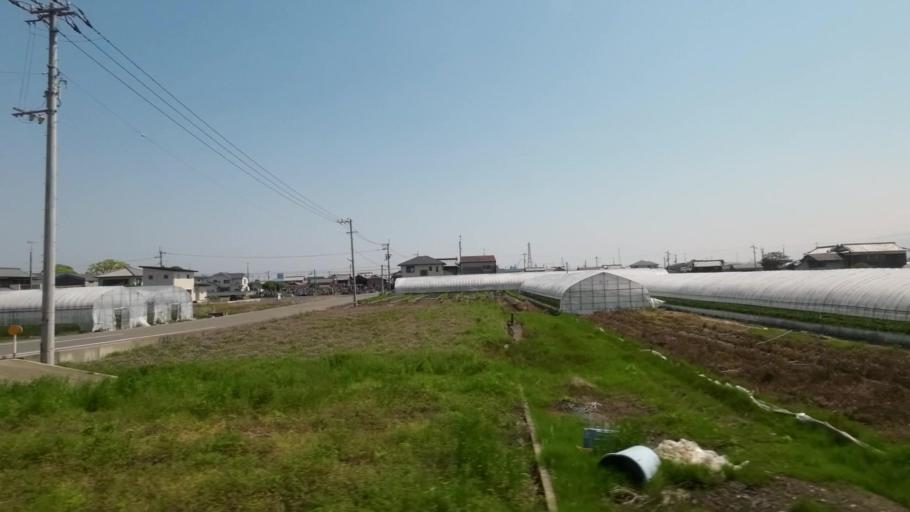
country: JP
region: Ehime
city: Saijo
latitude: 33.9238
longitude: 133.0908
